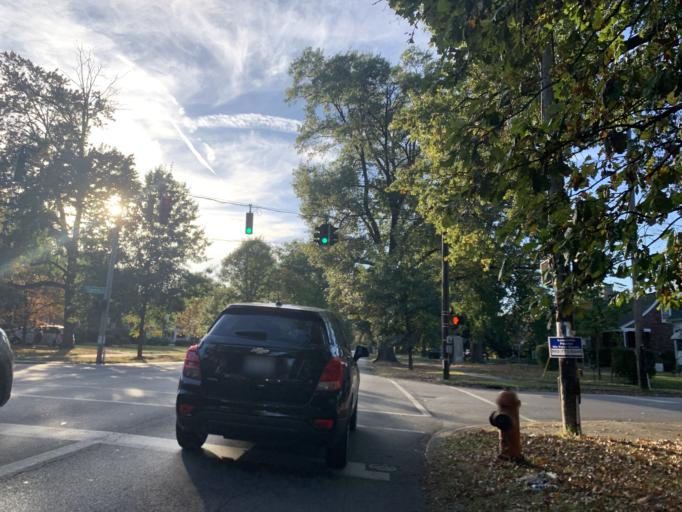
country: US
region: Kentucky
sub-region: Jefferson County
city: Shively
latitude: 38.2238
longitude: -85.8000
